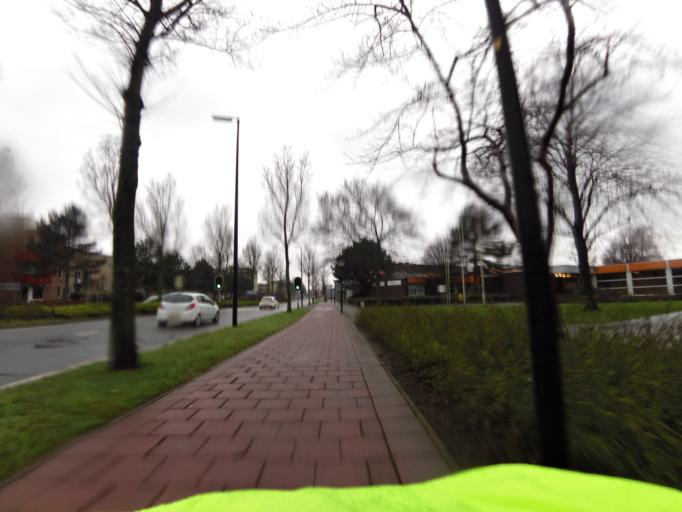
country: NL
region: South Holland
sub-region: Gemeente Maassluis
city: Maassluis
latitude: 51.9293
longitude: 4.2431
